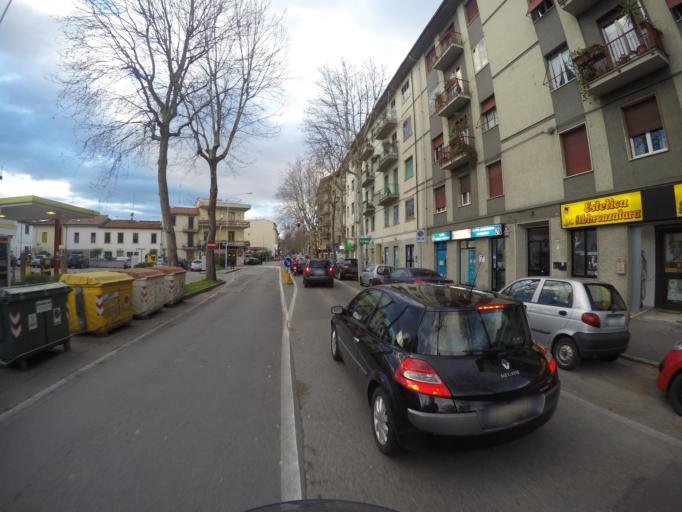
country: IT
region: Tuscany
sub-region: Provincia di Prato
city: Prato
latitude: 43.8696
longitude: 11.1116
